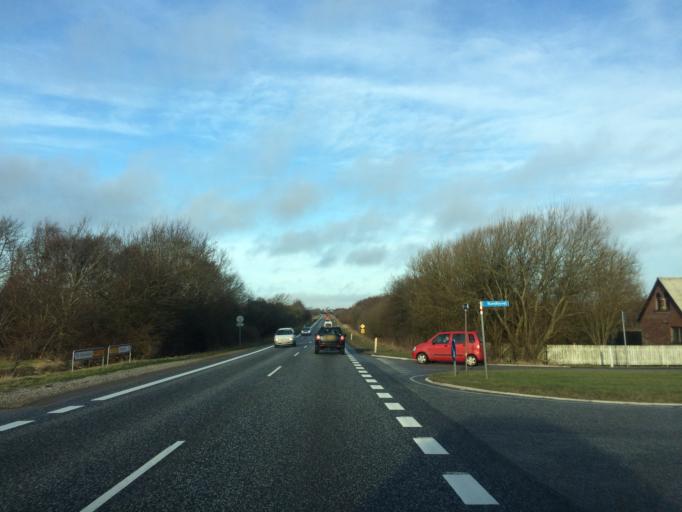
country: DK
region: North Denmark
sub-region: Thisted Kommune
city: Thisted
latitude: 56.8890
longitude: 8.5969
